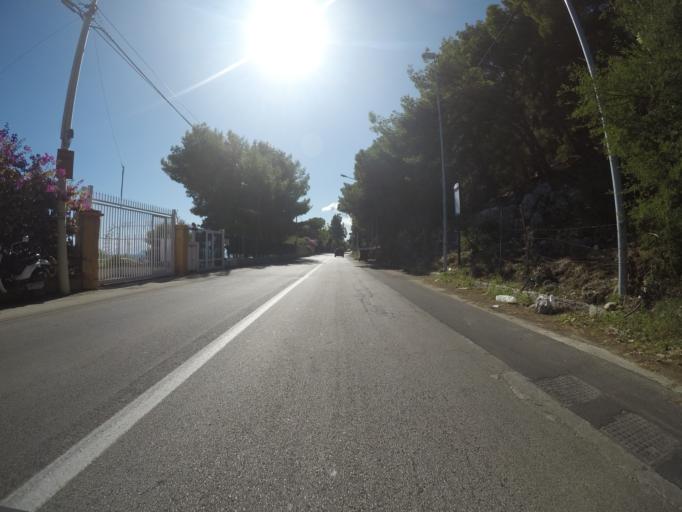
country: IT
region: Sicily
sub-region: Palermo
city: Palermo
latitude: 38.1827
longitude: 13.3646
